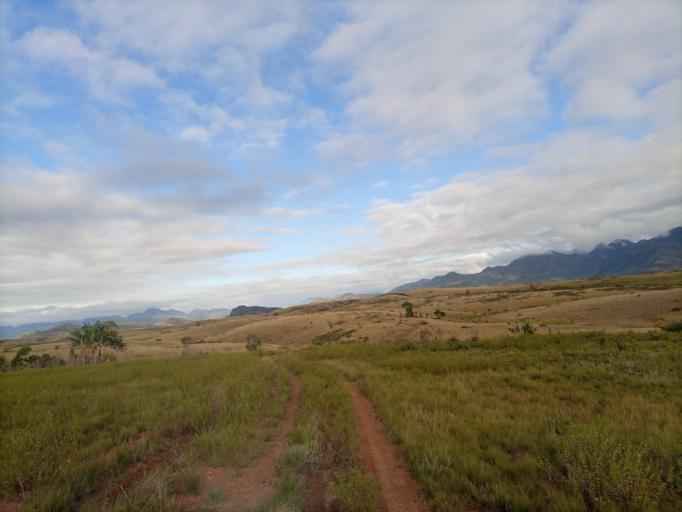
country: MG
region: Anosy
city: Fort Dauphin
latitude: -24.3091
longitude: 47.2463
